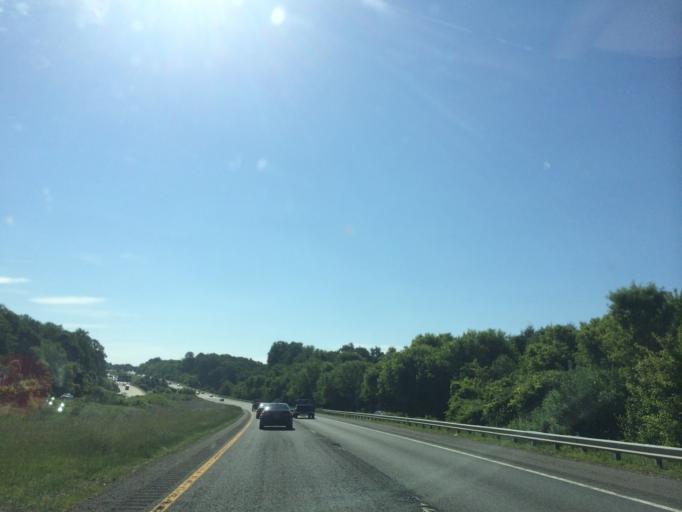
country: US
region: Maryland
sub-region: Howard County
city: Riverside
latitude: 39.1841
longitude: -76.8952
